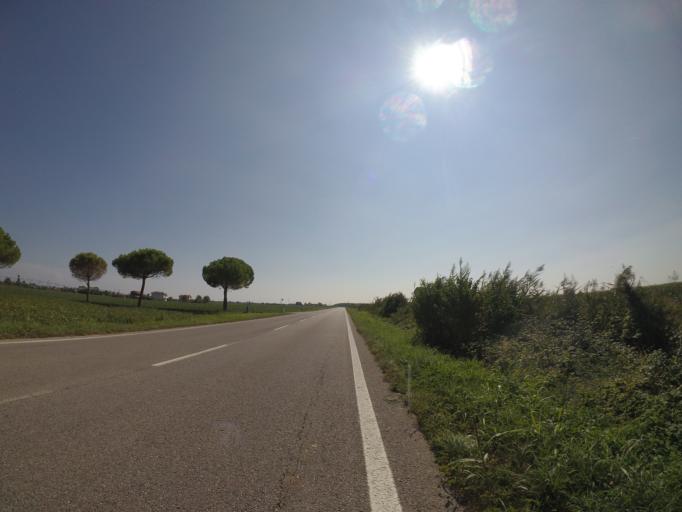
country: IT
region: Friuli Venezia Giulia
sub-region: Provincia di Udine
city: Marano Lagunare
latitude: 45.7873
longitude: 13.1643
